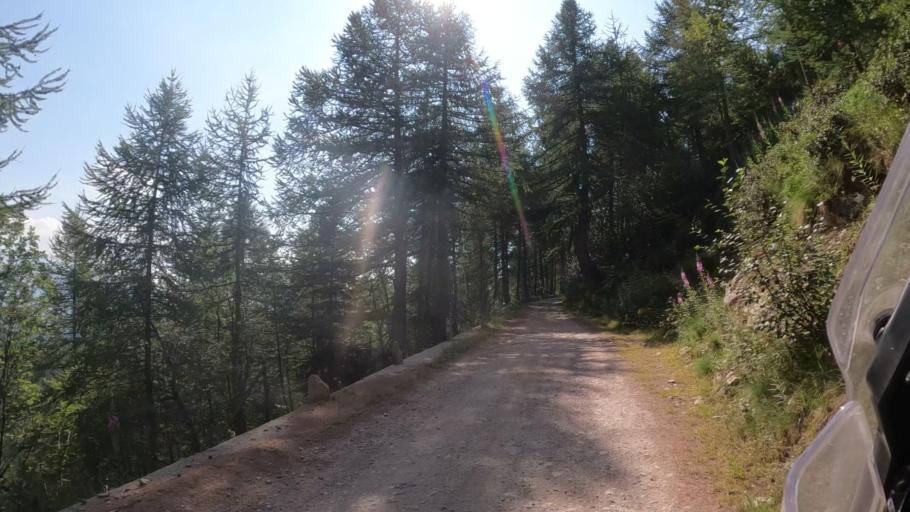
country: IT
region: Piedmont
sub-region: Provincia di Cuneo
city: Briga Alta
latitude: 44.1081
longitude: 7.7049
